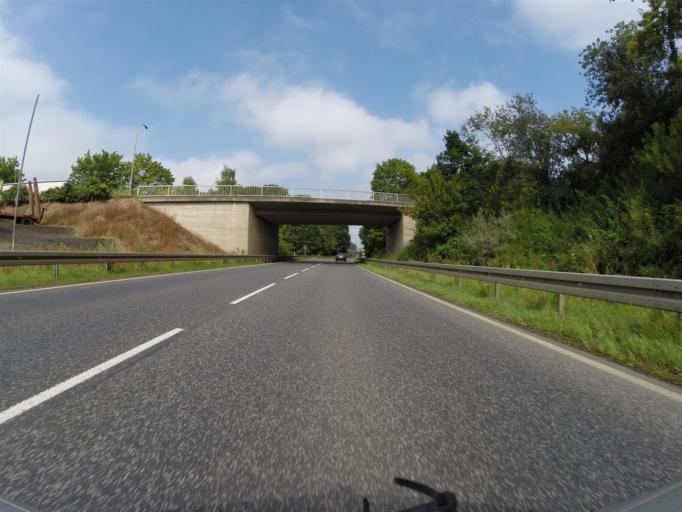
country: DE
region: Hesse
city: Waldkappel
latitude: 51.1482
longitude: 9.8803
